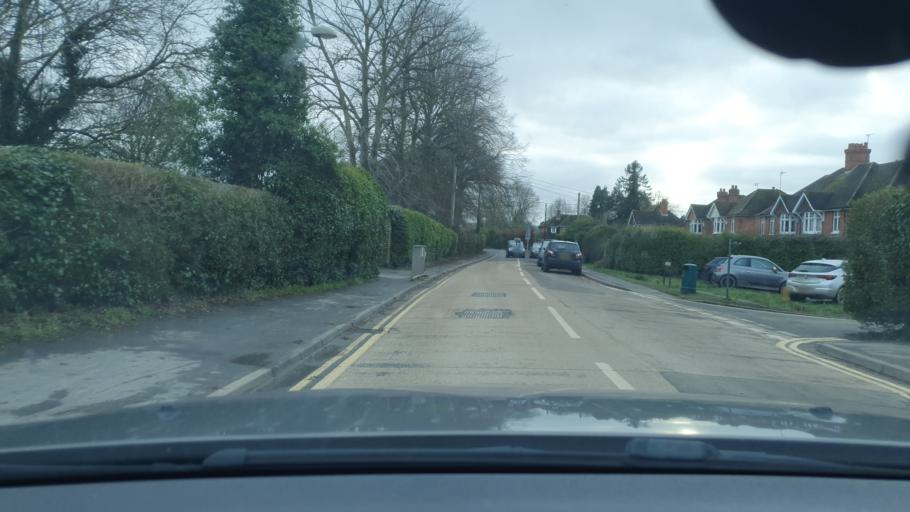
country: GB
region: England
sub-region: Oxfordshire
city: Wantage
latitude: 51.5843
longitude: -1.4262
